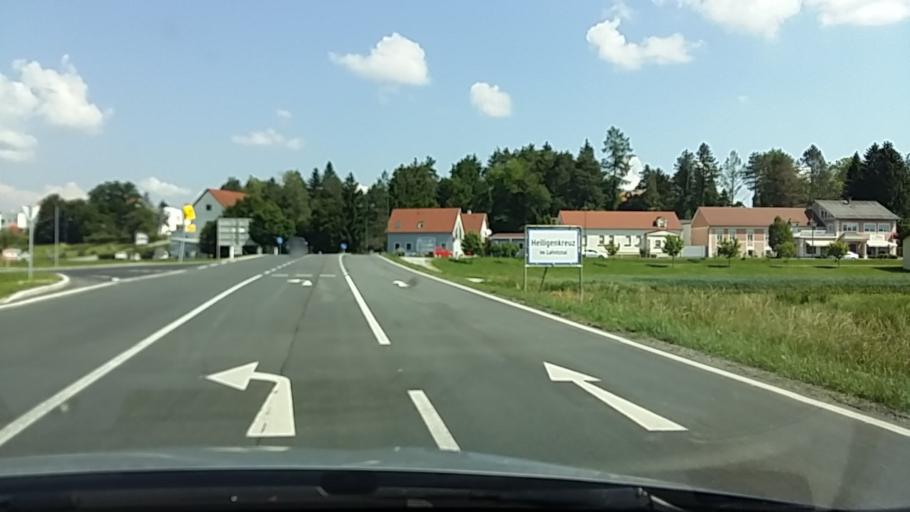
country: AT
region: Burgenland
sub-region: Politischer Bezirk Jennersdorf
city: Heiligenkreuz im Lafnitztal
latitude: 46.9870
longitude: 16.2538
